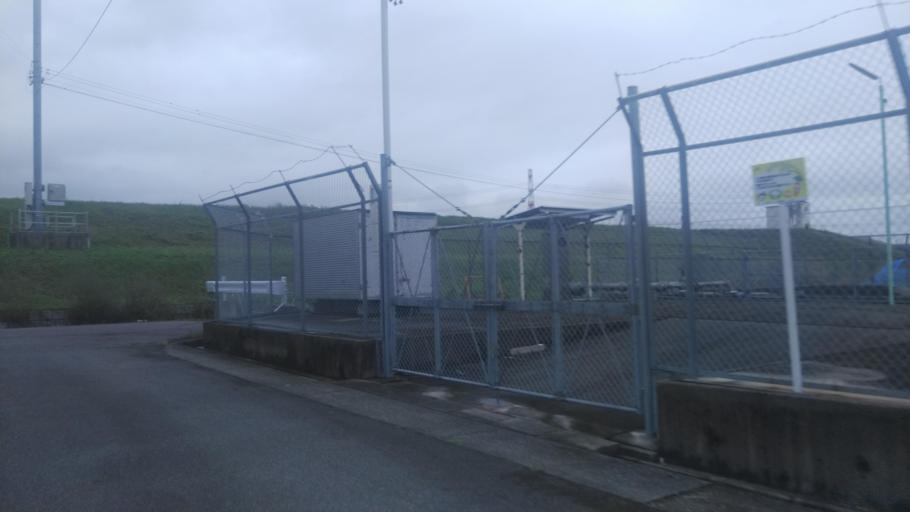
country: JP
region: Aichi
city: Kasugai
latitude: 35.2509
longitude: 137.0181
